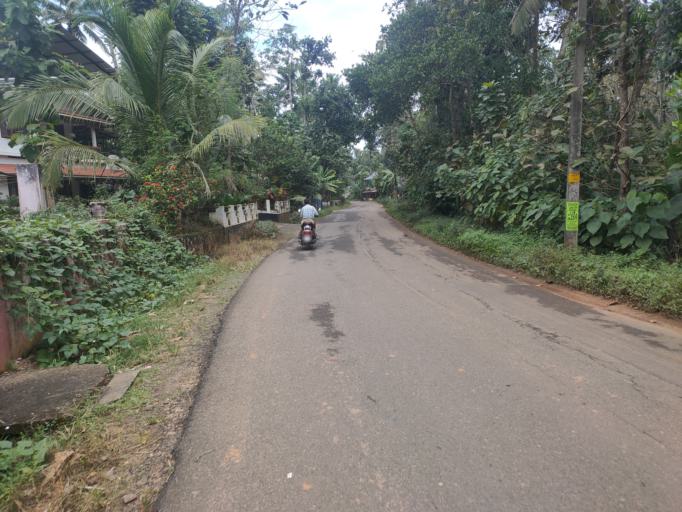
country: IN
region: Kerala
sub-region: Ernakulam
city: Muvattupula
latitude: 9.9872
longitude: 76.6370
